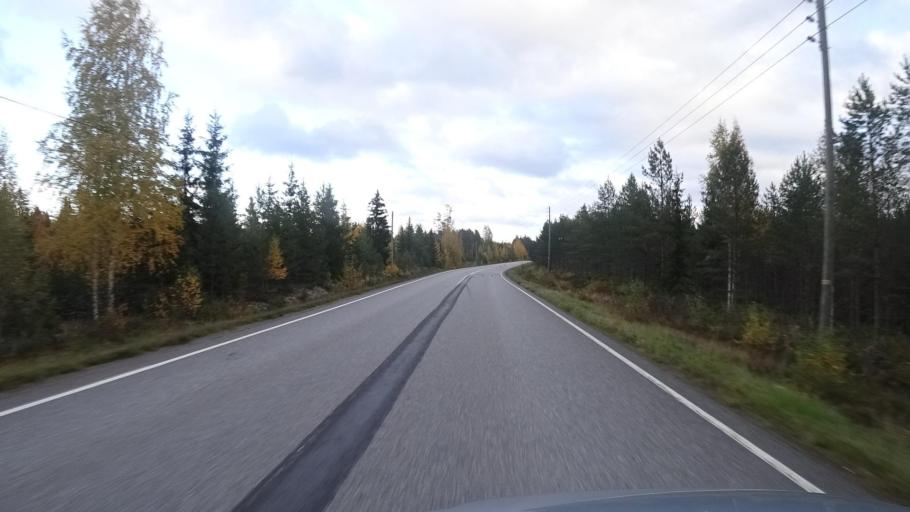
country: FI
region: Varsinais-Suomi
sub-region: Loimaa
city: Ylaene
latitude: 60.9947
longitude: 22.5073
